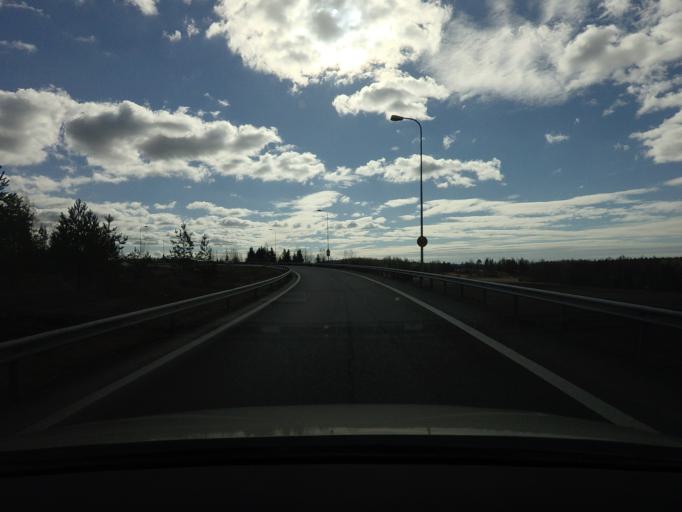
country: FI
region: Uusimaa
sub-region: Loviisa
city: Perna
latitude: 60.4904
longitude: 25.9532
